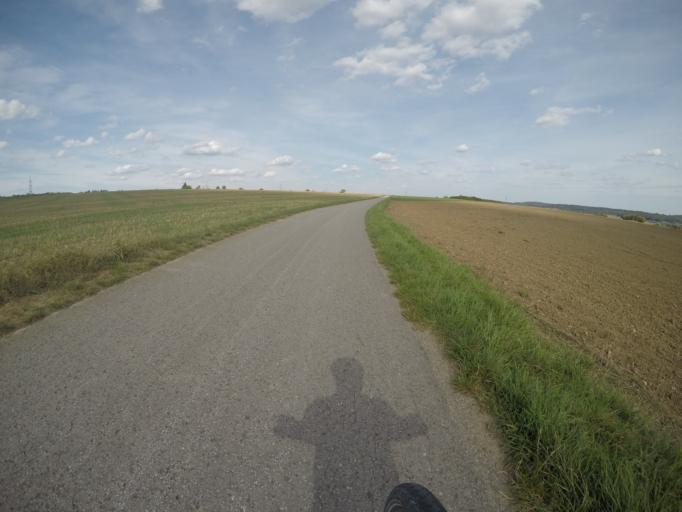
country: DE
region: Baden-Wuerttemberg
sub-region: Regierungsbezirk Stuttgart
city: Gartringen
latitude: 48.6497
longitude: 8.9020
